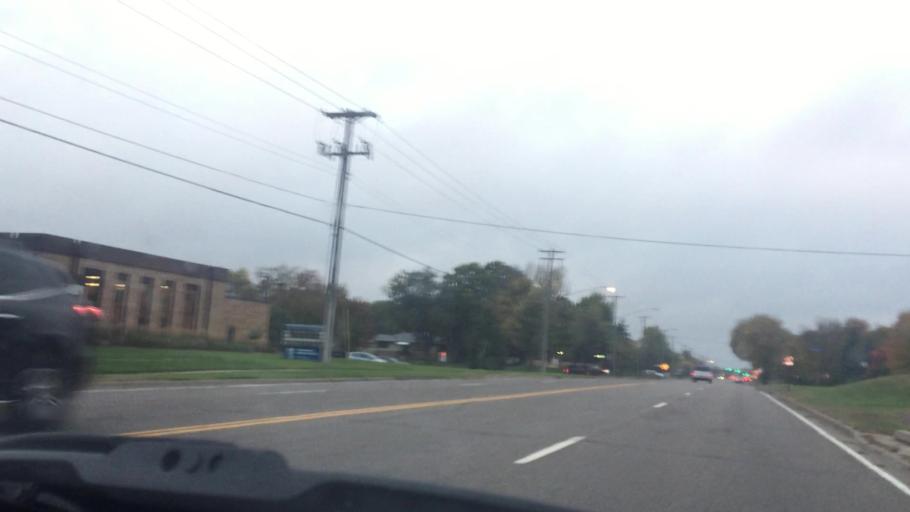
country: US
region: Minnesota
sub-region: Anoka County
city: Spring Lake Park
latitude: 45.1079
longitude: -93.2487
